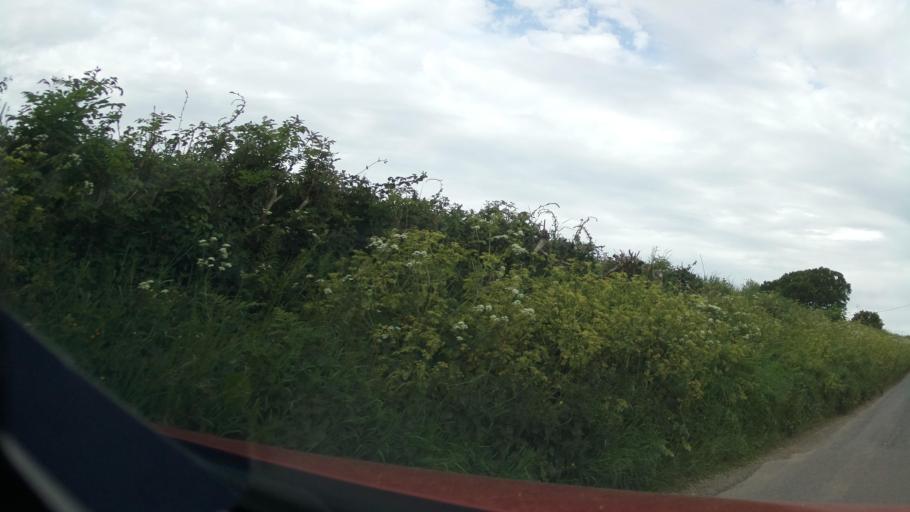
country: GB
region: England
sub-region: Devon
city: Dartmouth
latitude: 50.3445
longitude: -3.6554
